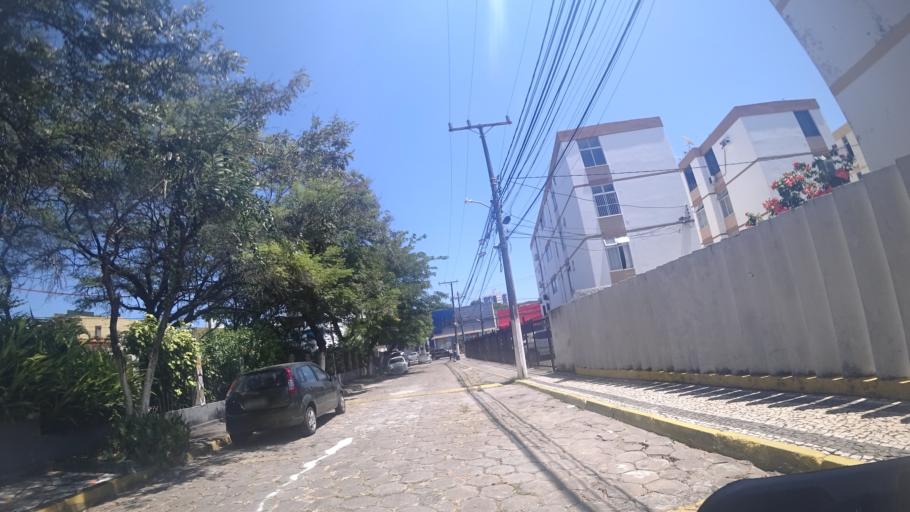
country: BR
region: Bahia
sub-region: Salvador
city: Salvador
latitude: -12.9894
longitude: -38.4579
